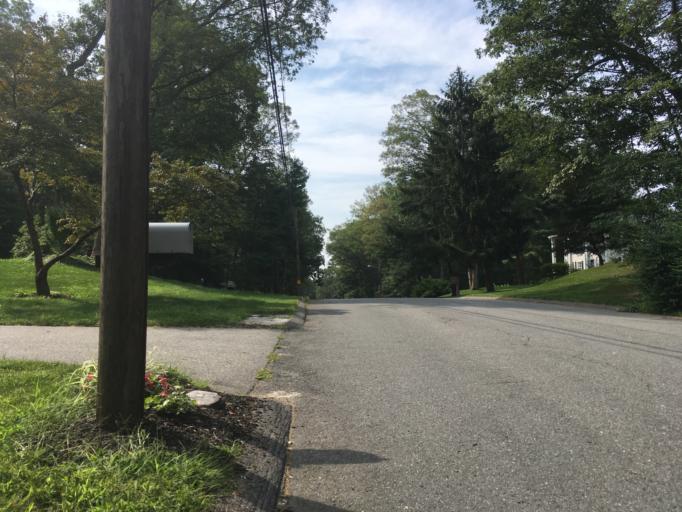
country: US
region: Rhode Island
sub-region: Kent County
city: East Greenwich
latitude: 41.6375
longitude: -71.4781
